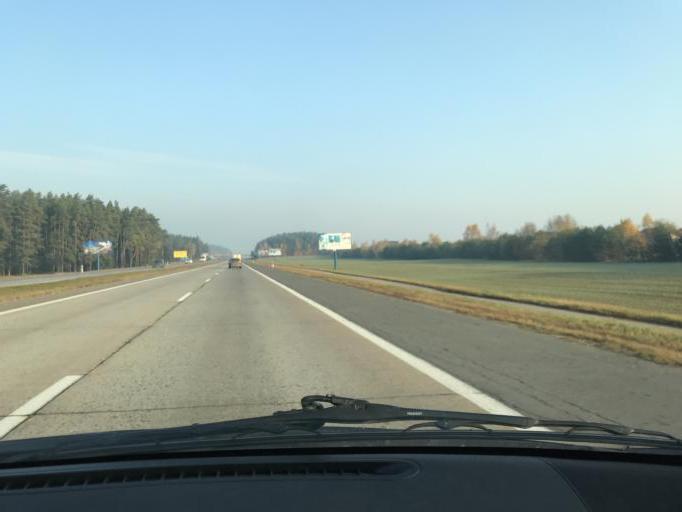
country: BY
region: Minsk
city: Borovlyany
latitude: 53.9947
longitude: 27.6572
